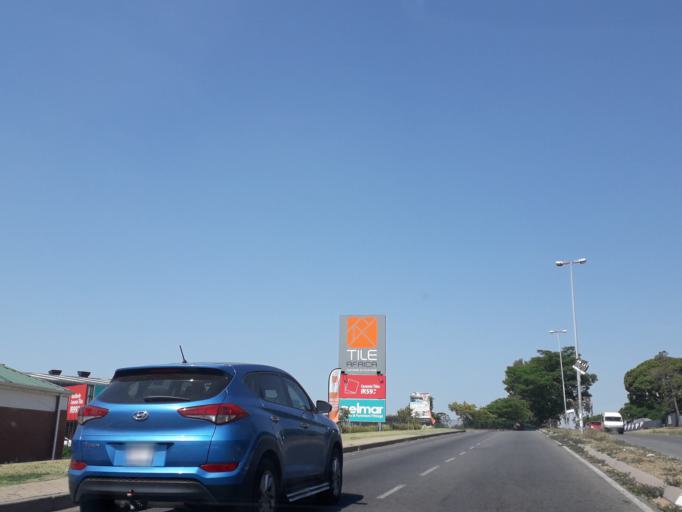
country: ZA
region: Gauteng
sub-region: City of Johannesburg Metropolitan Municipality
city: Roodepoort
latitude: -26.0796
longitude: 27.9783
